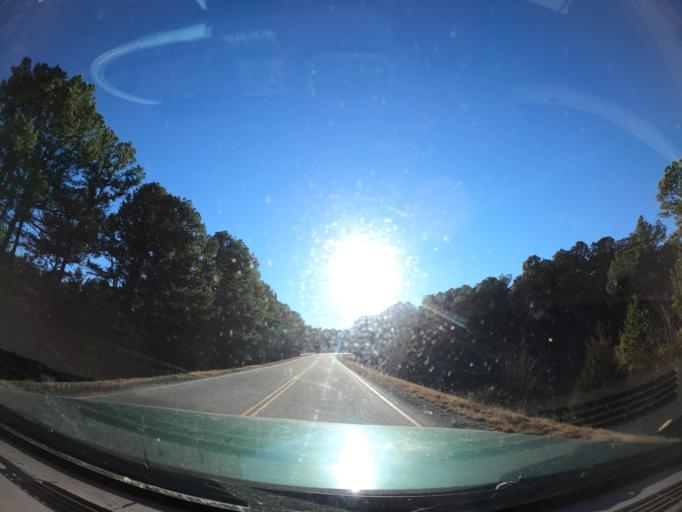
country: US
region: Oklahoma
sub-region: Latimer County
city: Wilburton
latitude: 35.0028
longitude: -95.3337
